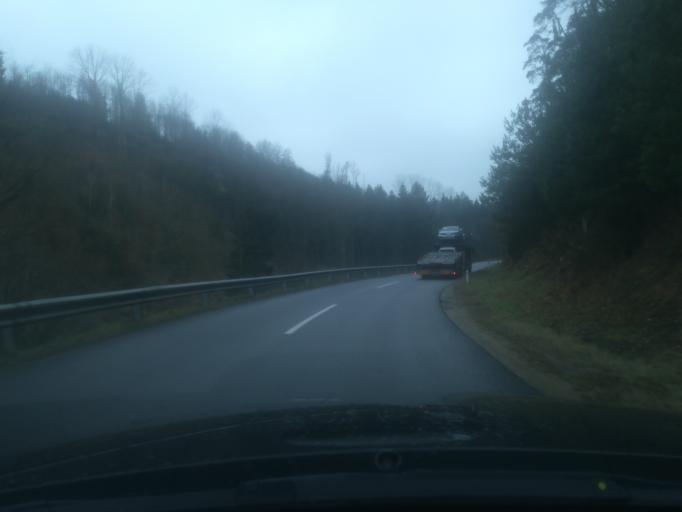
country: AT
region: Upper Austria
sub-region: Politischer Bezirk Perg
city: Perg
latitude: 48.3183
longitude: 14.5810
